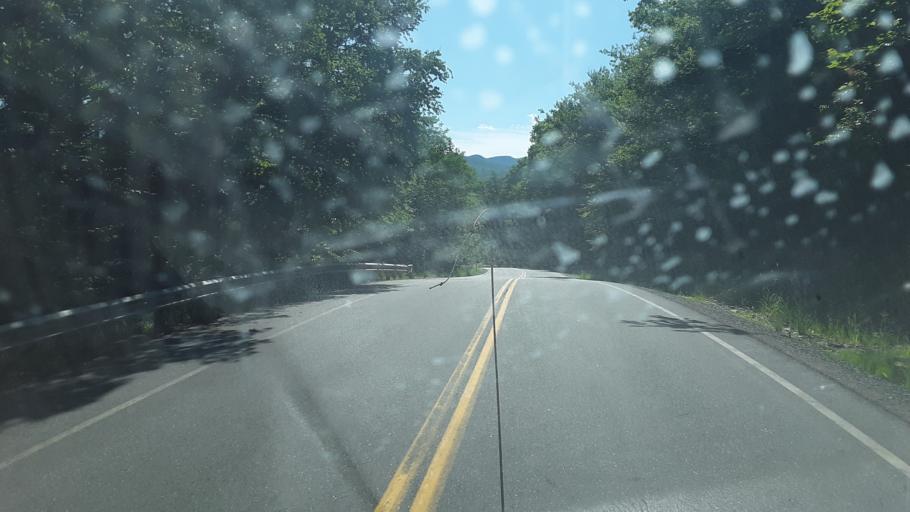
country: US
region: New Hampshire
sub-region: Grafton County
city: North Haverhill
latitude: 44.0981
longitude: -71.8525
